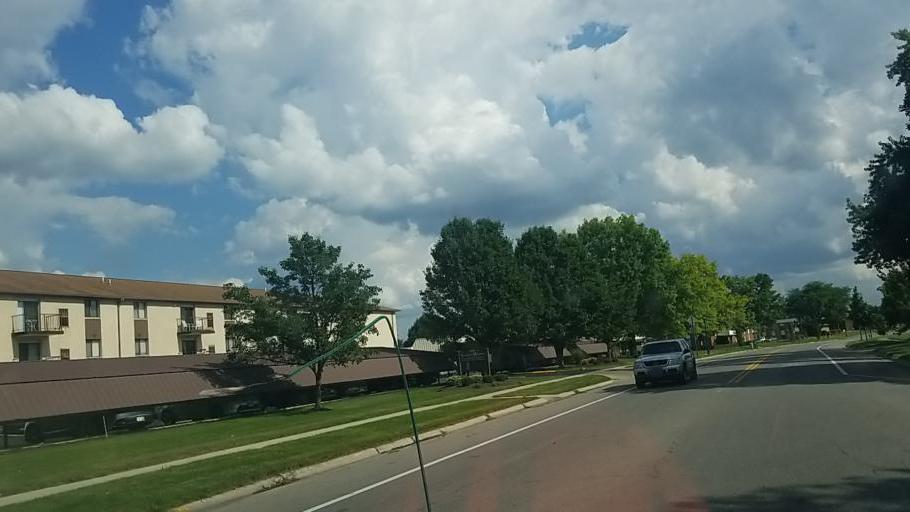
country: US
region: Ohio
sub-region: Franklin County
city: Minerva Park
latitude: 40.0899
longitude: -82.9702
